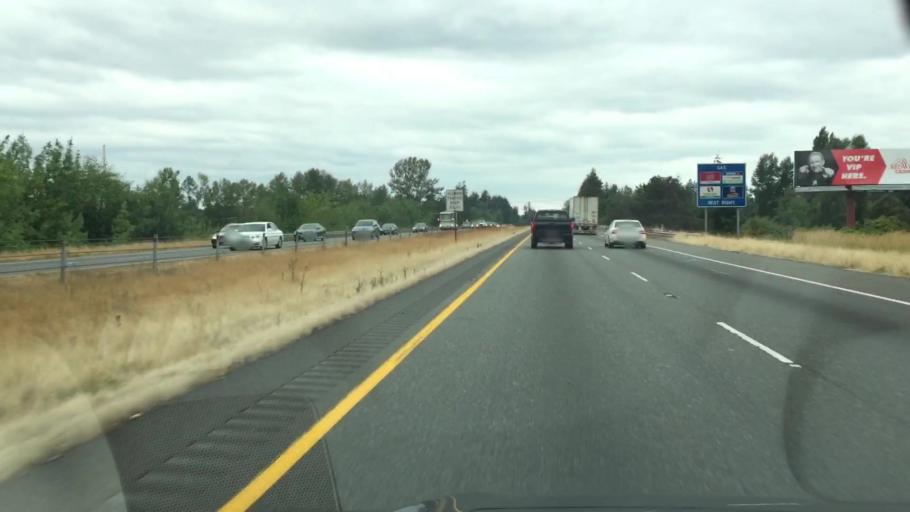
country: US
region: Washington
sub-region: Pierce County
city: Midland
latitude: 47.1583
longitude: -122.3845
